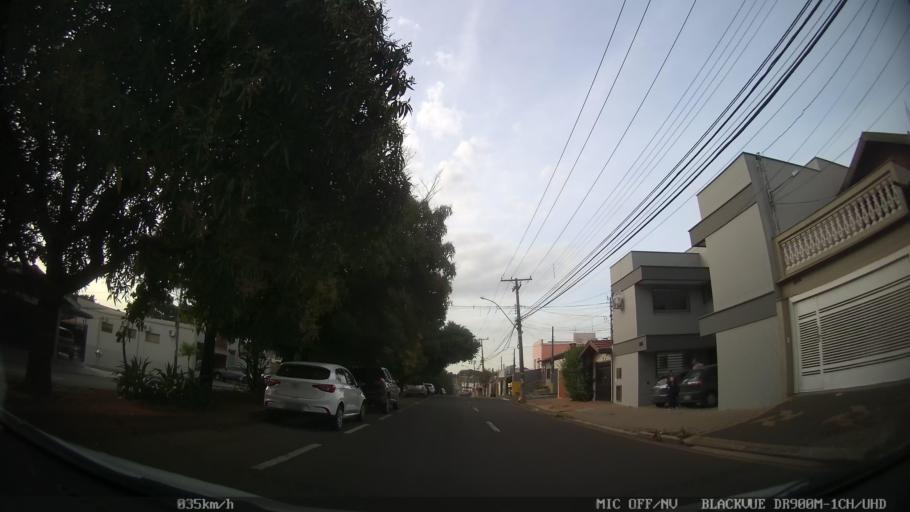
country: BR
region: Sao Paulo
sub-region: Piracicaba
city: Piracicaba
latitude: -22.7363
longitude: -47.6234
